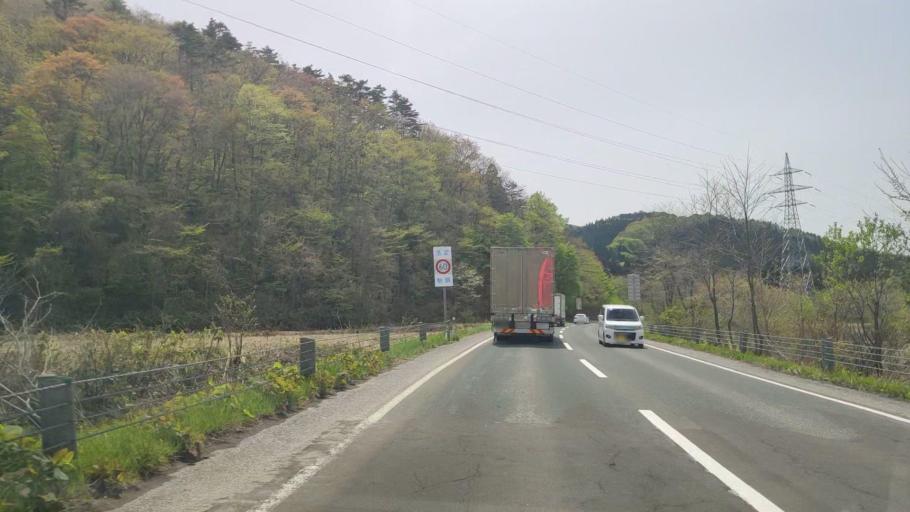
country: JP
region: Aomori
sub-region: Misawa Shi
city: Inuotose
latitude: 40.7890
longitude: 141.0850
